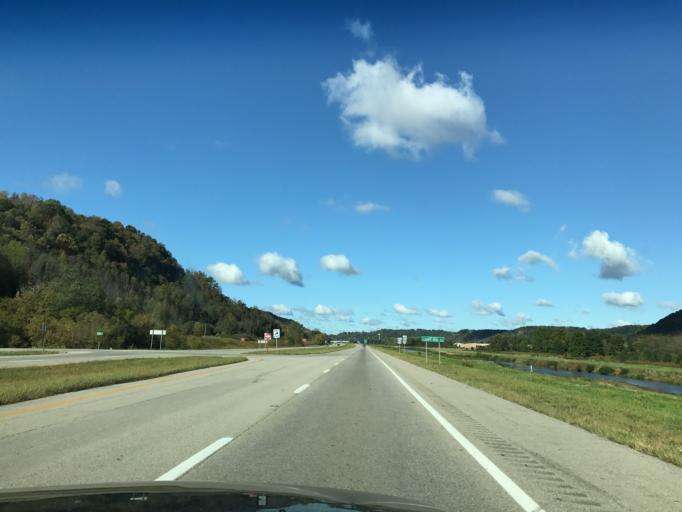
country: US
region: Ohio
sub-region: Athens County
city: Athens
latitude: 39.3317
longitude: -82.0520
